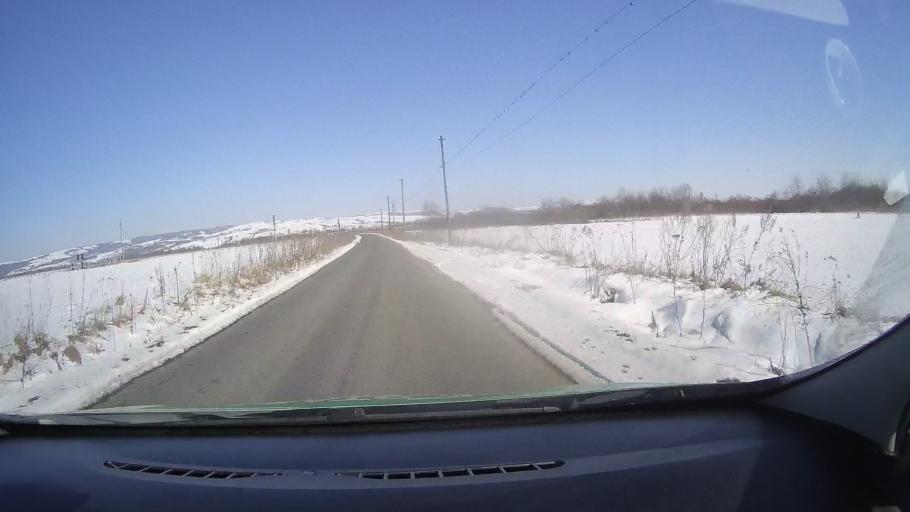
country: RO
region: Brasov
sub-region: Comuna Mandra
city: Mandra
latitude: 45.8288
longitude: 25.0120
